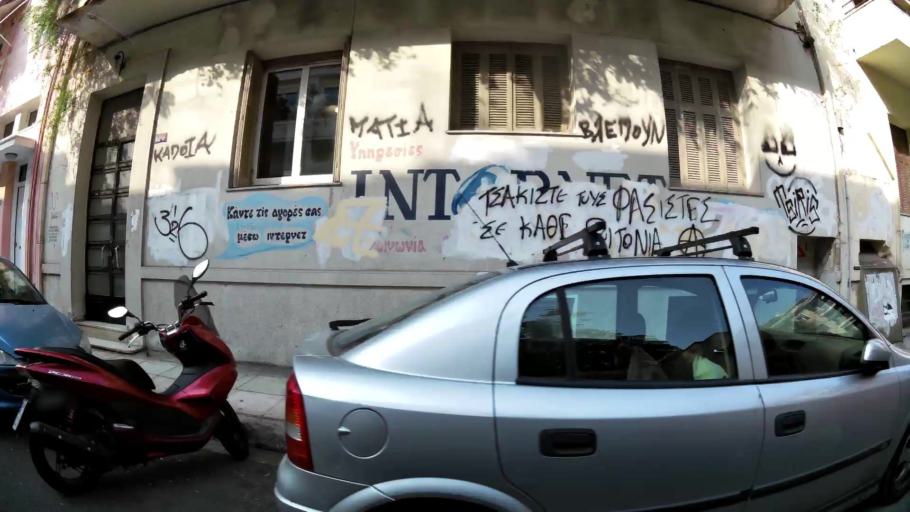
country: GR
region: Attica
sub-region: Nomarchia Athinas
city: Kipseli
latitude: 38.0056
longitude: 23.7360
